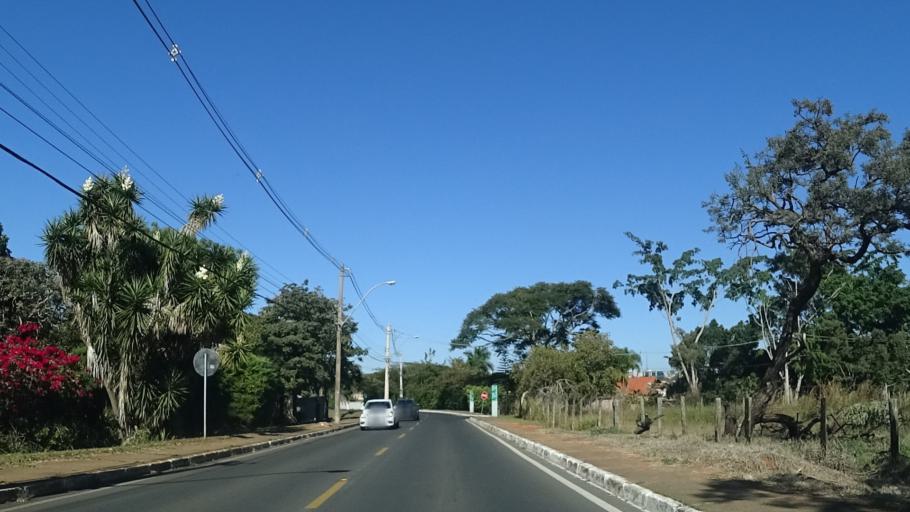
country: BR
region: Federal District
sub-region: Brasilia
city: Brasilia
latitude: -15.7534
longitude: -47.8425
